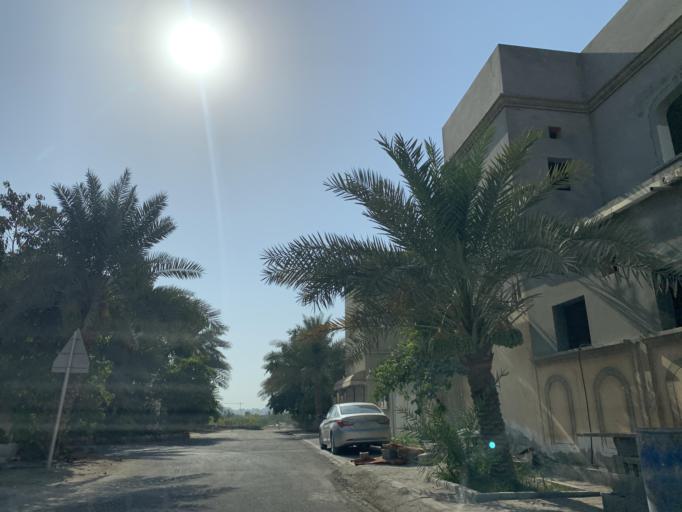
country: BH
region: Manama
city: Jidd Hafs
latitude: 26.1973
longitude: 50.5166
